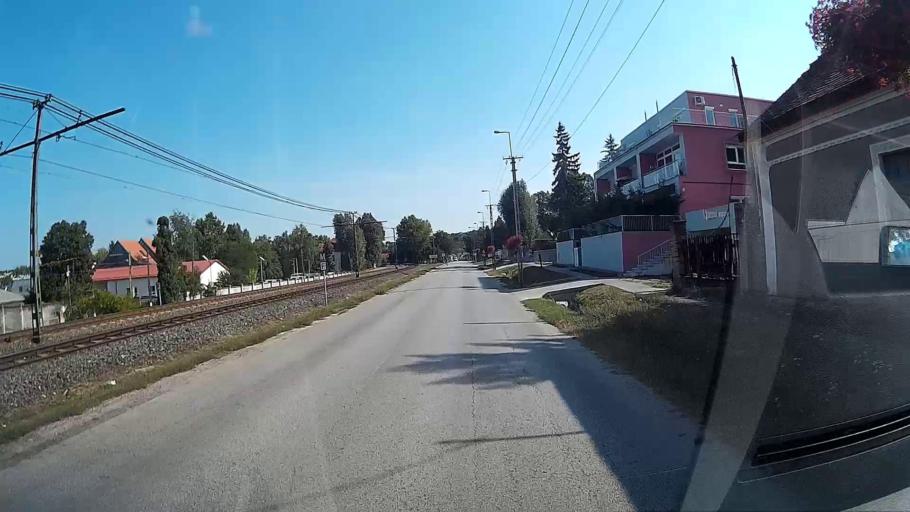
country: HU
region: Pest
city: Budakalasz
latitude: 47.6244
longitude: 19.0450
